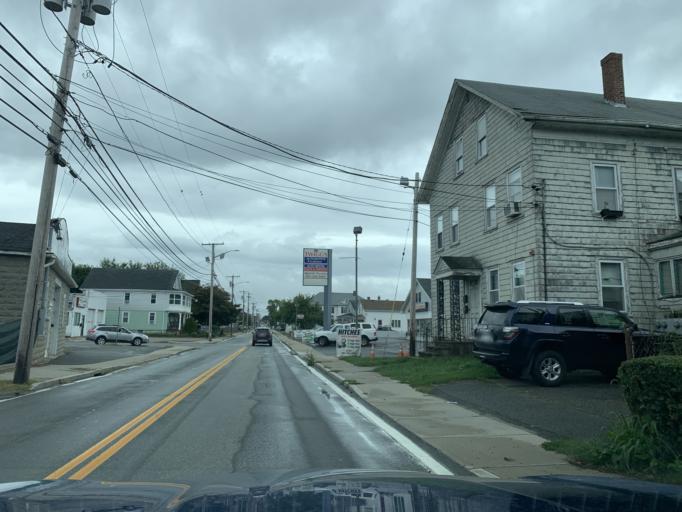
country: US
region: Rhode Island
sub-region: Bristol County
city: Warren
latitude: 41.7298
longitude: -71.2765
